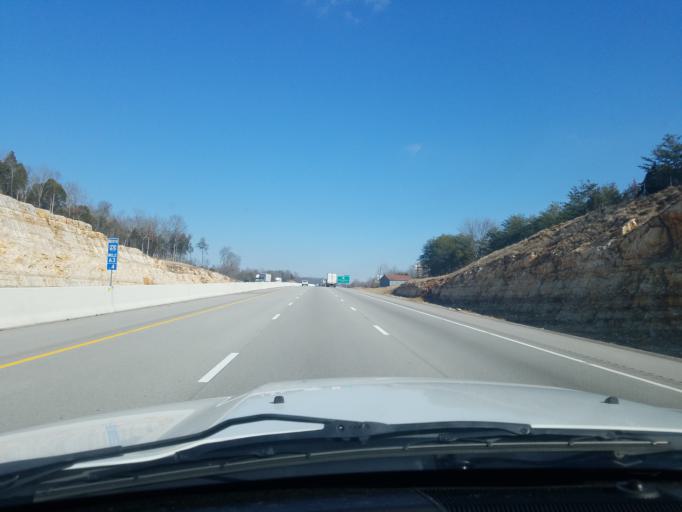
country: US
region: Kentucky
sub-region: Hart County
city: Munfordville
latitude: 37.2824
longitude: -85.9087
